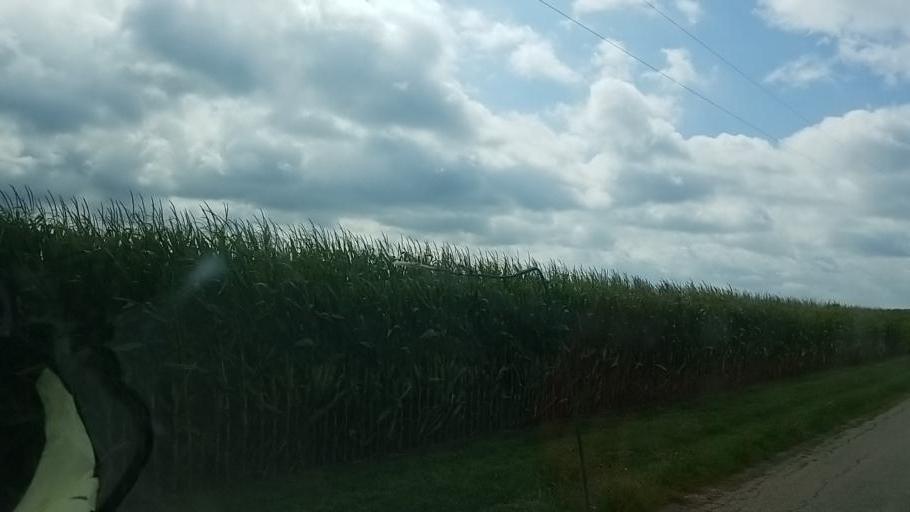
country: US
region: Ohio
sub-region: Madison County
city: Mount Sterling
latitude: 39.7705
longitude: -83.2667
